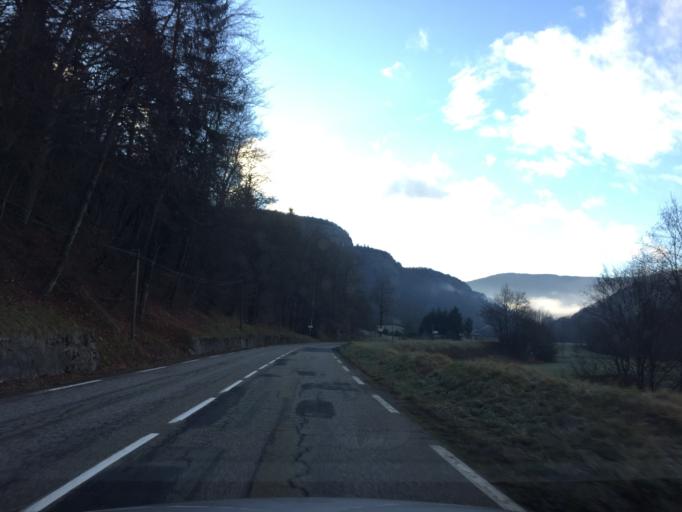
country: FR
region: Rhone-Alpes
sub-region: Departement de la Haute-Savoie
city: Gruffy
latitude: 45.7419
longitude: 6.0981
